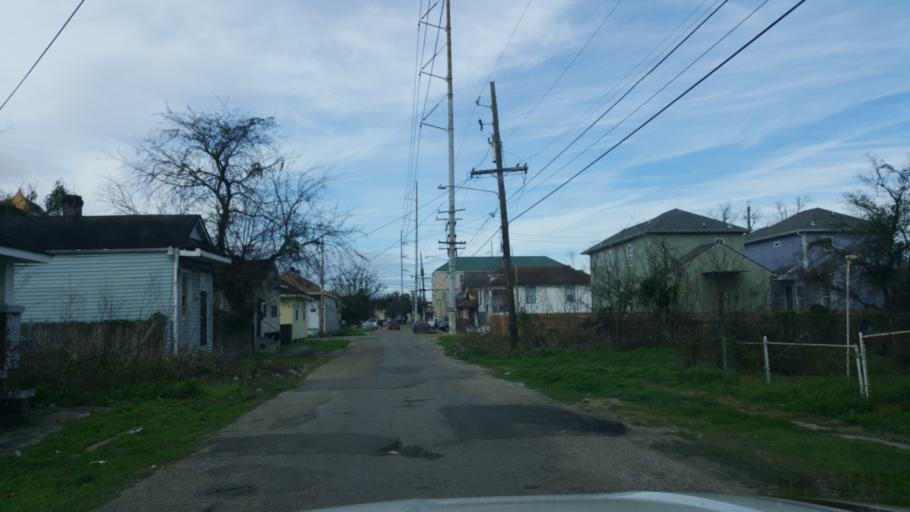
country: US
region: Louisiana
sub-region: Orleans Parish
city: New Orleans
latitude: 29.9752
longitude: -90.0649
